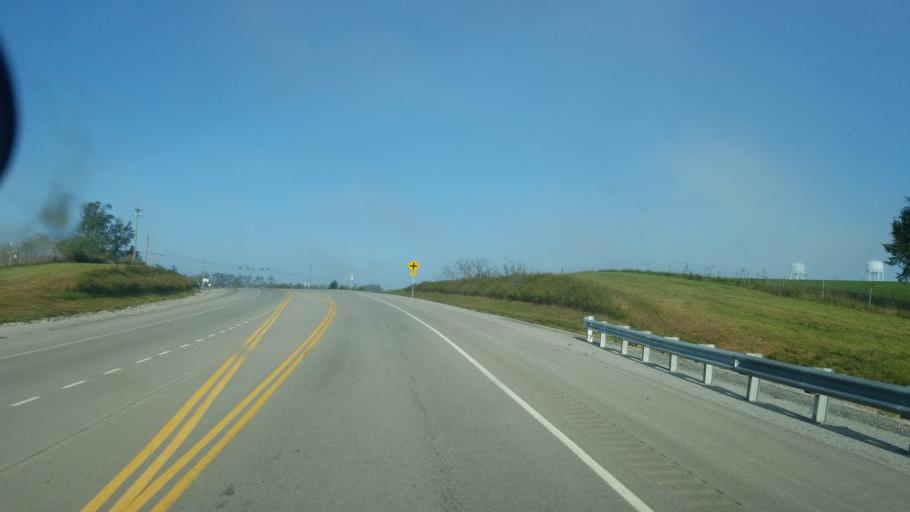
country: US
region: Kentucky
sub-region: Fleming County
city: Flemingsburg
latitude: 38.4412
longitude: -83.7275
